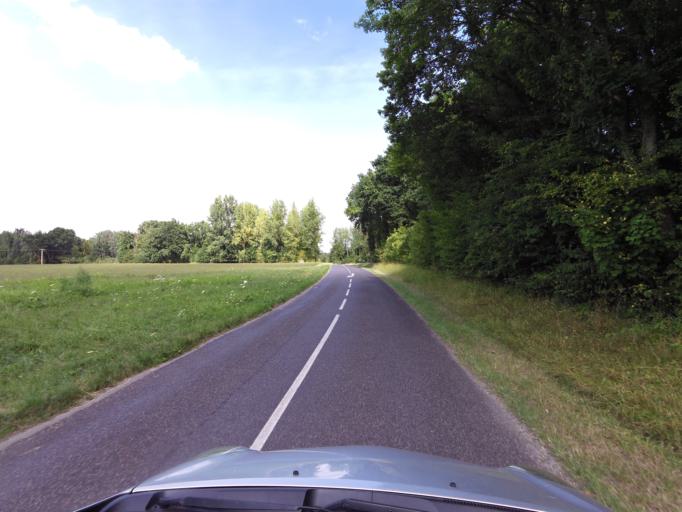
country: FR
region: Picardie
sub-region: Departement de l'Aisne
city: Bruyeres-et-Montberault
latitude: 49.5039
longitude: 3.6156
